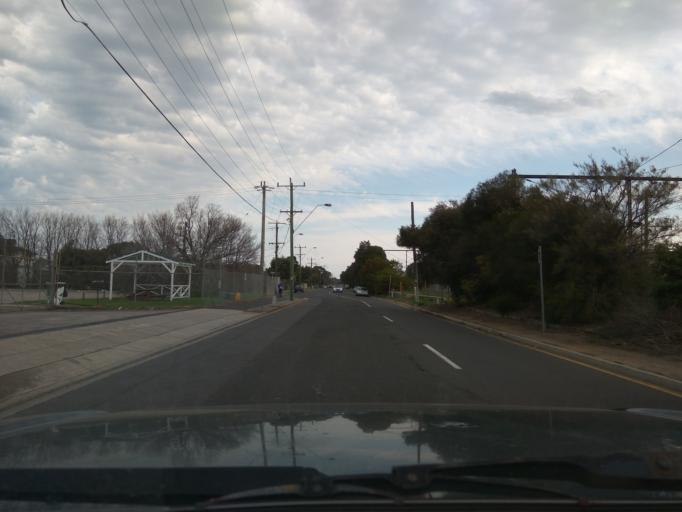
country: AU
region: Victoria
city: Spotswood
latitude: -37.8310
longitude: 144.8861
